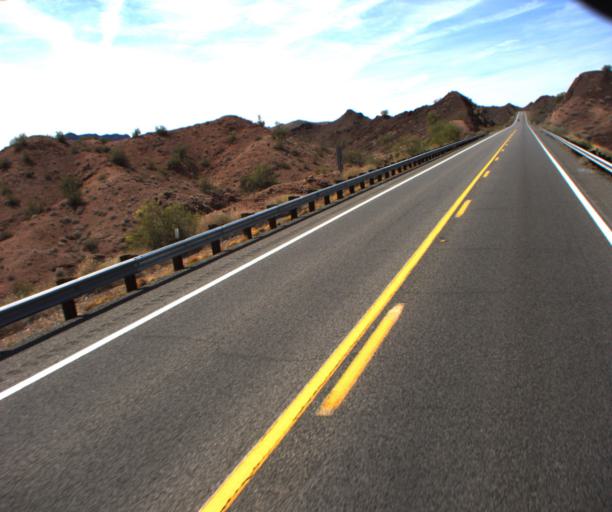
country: US
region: Arizona
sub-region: La Paz County
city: Cienega Springs
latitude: 34.3116
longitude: -114.1052
